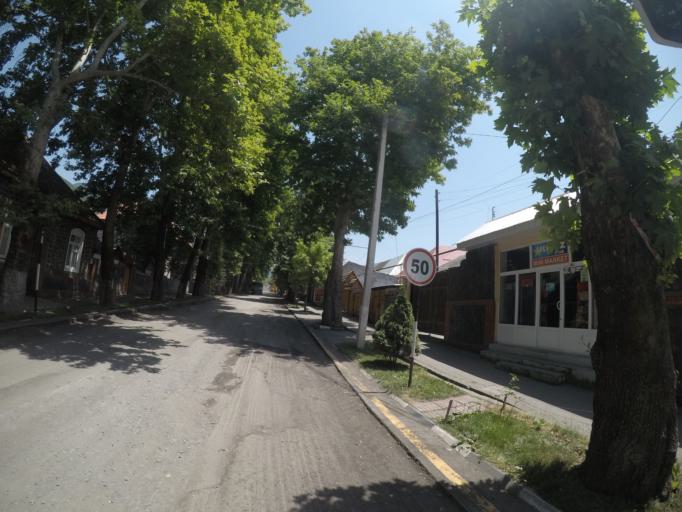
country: AZ
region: Qakh Rayon
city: Qax
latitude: 41.4211
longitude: 46.9266
